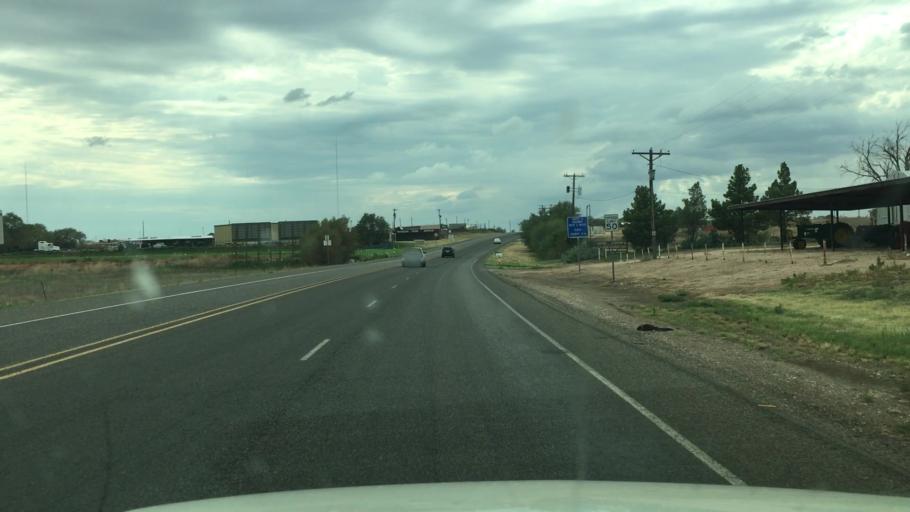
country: US
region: Texas
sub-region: Terry County
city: Brownfield
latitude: 33.1791
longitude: -102.2930
